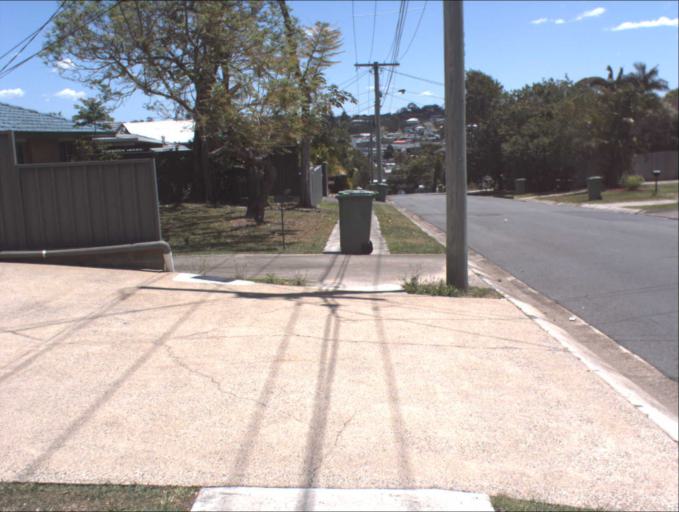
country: AU
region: Queensland
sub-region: Logan
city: Springwood
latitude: -27.6075
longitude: 153.1182
